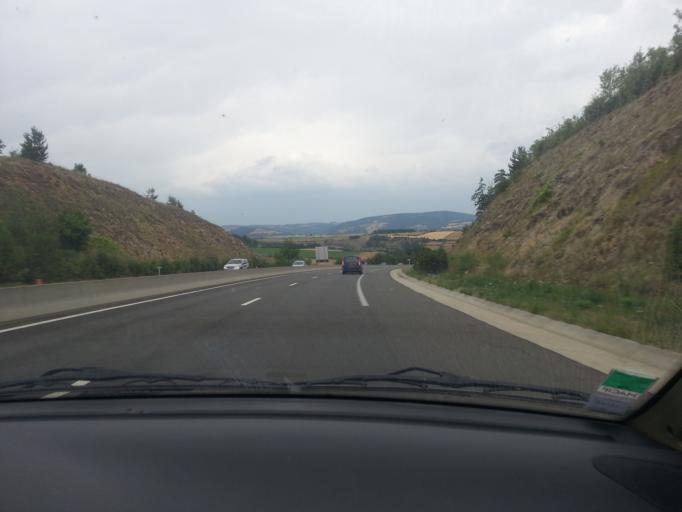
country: FR
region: Languedoc-Roussillon
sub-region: Departement de la Lozere
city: Chirac
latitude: 44.5261
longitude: 3.2428
